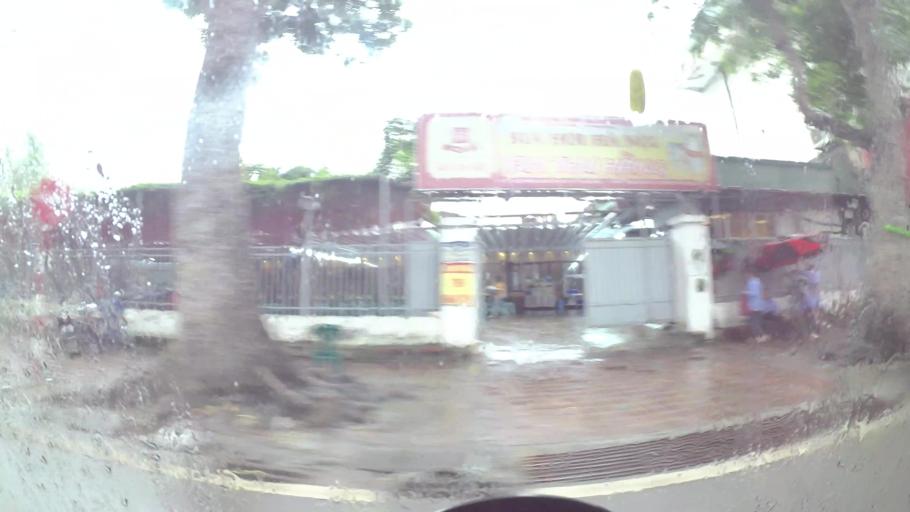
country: VN
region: Ha Noi
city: Hai BaTrung
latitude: 21.0149
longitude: 105.8533
